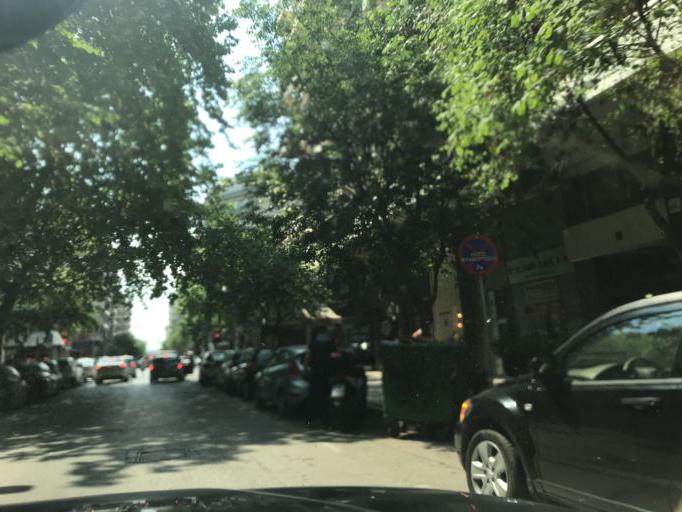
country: GR
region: Central Macedonia
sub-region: Nomos Thessalonikis
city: Agios Pavlos
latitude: 40.6306
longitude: 22.9474
